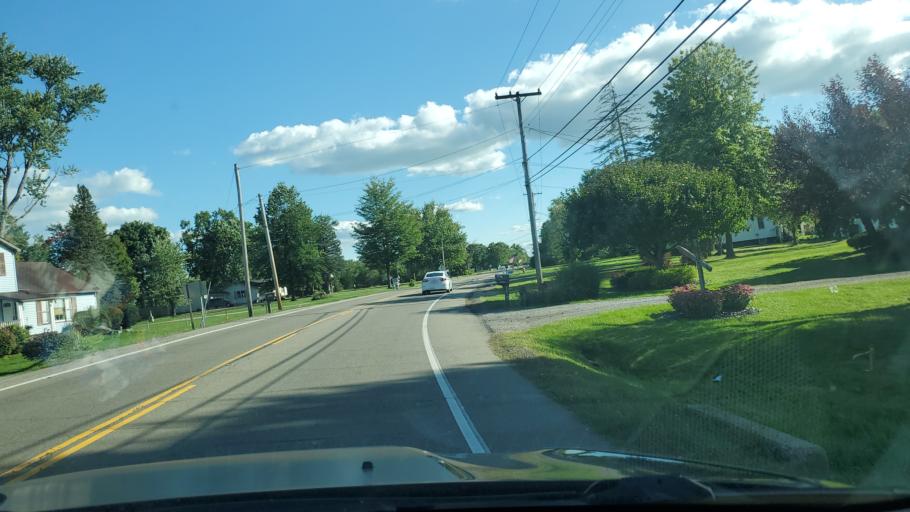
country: US
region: Ohio
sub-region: Mahoning County
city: Austintown
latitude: 41.0671
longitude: -80.7607
